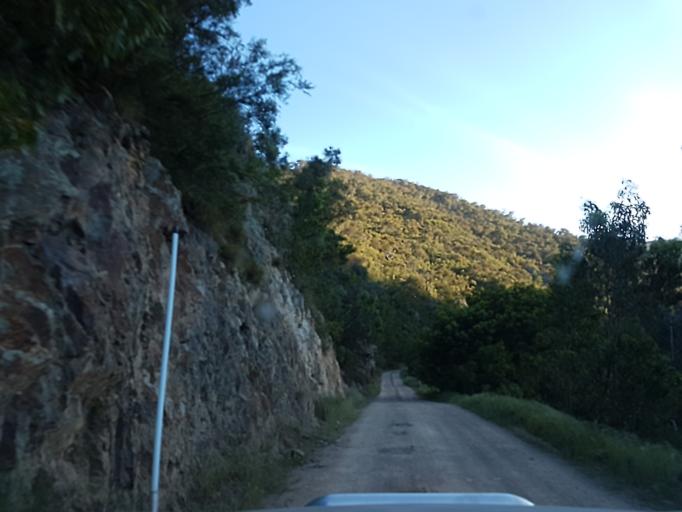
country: AU
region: Victoria
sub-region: Wellington
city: Heyfield
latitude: -37.4084
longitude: 147.0932
